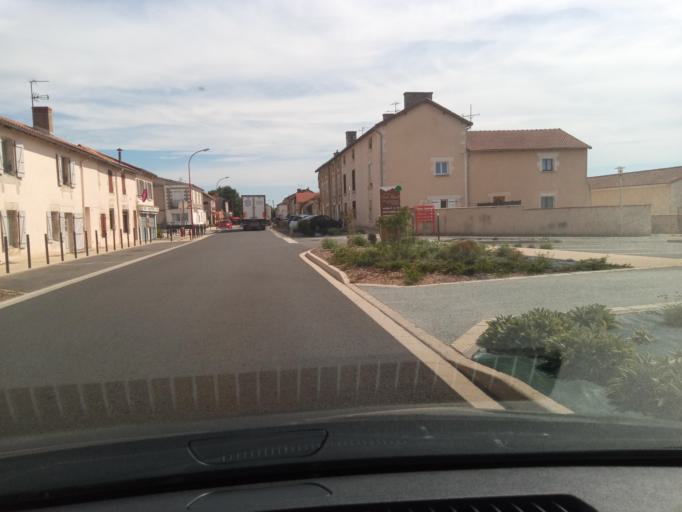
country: FR
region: Poitou-Charentes
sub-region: Departement de la Vienne
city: Terce
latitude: 46.4780
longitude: 0.5205
